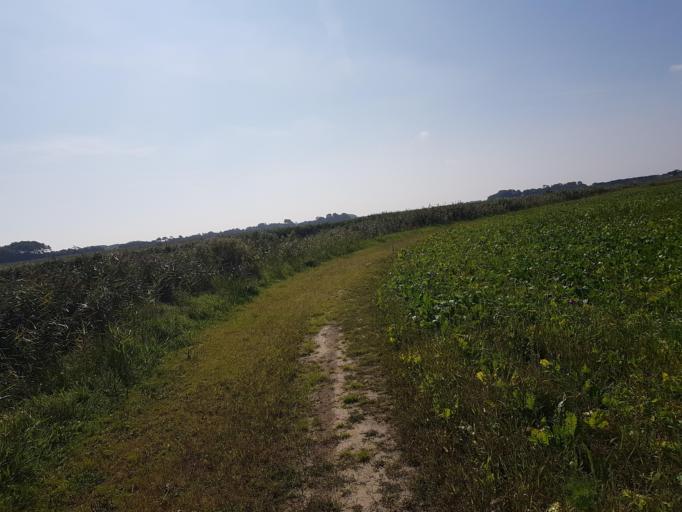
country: NL
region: North Holland
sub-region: Gemeente Texel
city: Den Burg
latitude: 53.0990
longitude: 4.8710
